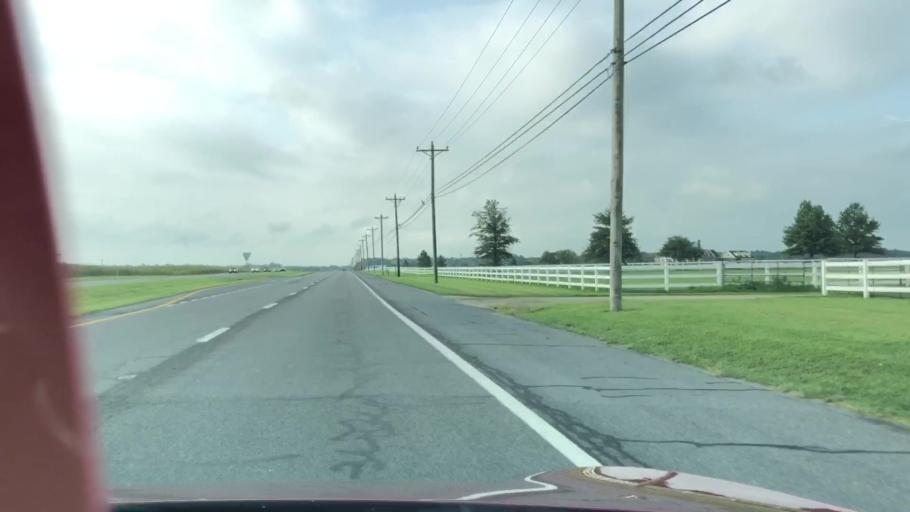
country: US
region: Delaware
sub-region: Kent County
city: Harrington
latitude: 38.9607
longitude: -75.5653
